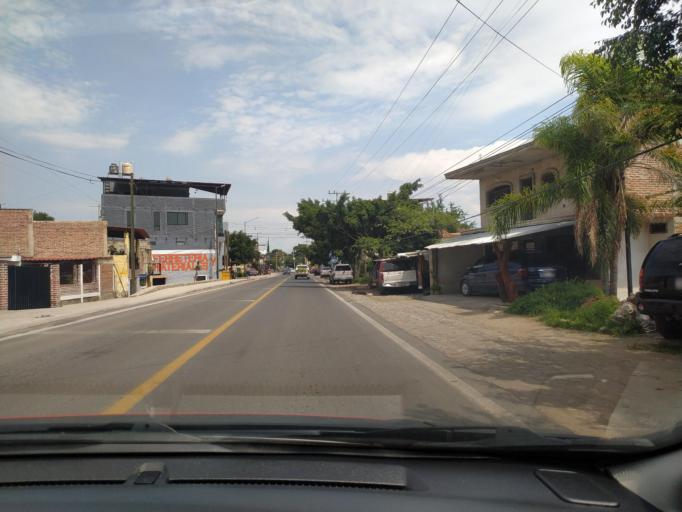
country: MX
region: Jalisco
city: San Juan Cosala
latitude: 20.2872
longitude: -103.3377
